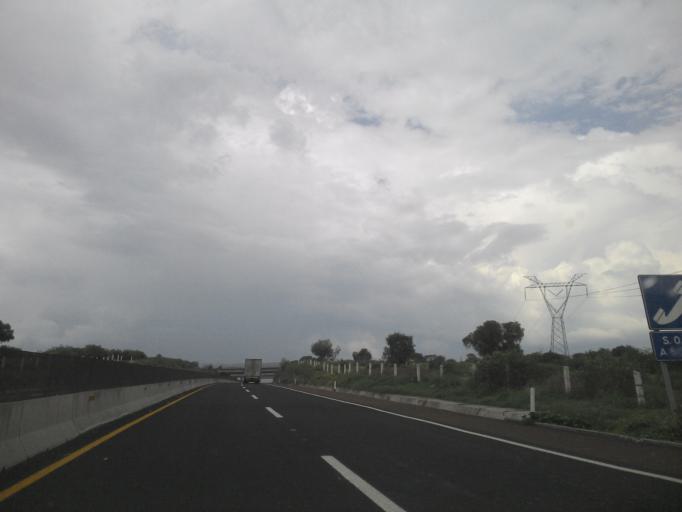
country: MX
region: Hidalgo
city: San Marcos
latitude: 20.0810
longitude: -99.3396
